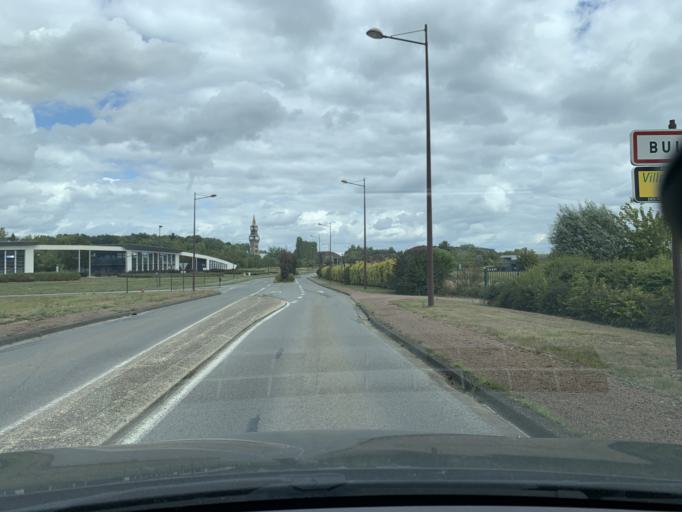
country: FR
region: Picardie
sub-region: Departement de l'Aisne
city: Hirson
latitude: 49.9074
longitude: 4.0716
